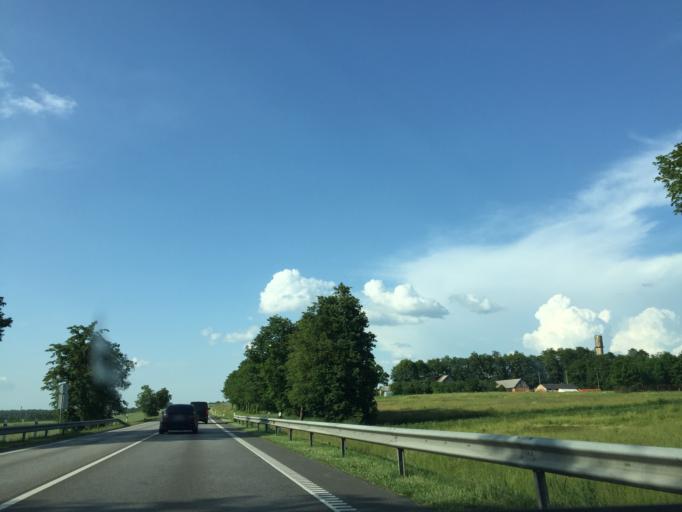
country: LT
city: Ramygala
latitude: 55.5813
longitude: 24.3387
